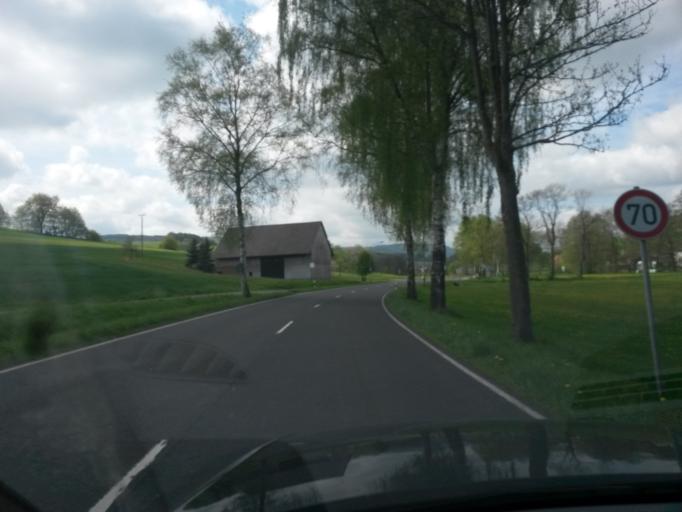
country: DE
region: Hesse
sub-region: Regierungsbezirk Kassel
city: Hilders
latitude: 50.5525
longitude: 10.0044
